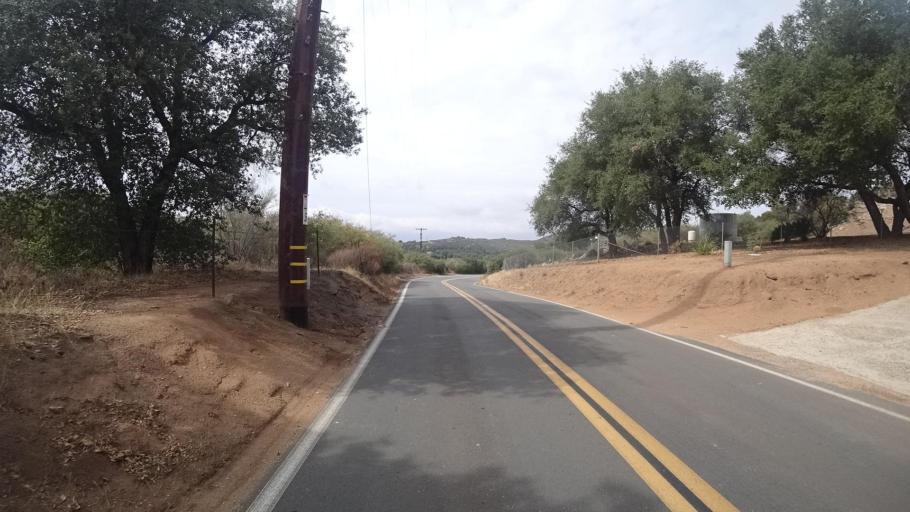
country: US
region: California
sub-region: San Diego County
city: Descanso
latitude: 32.8769
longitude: -116.6388
